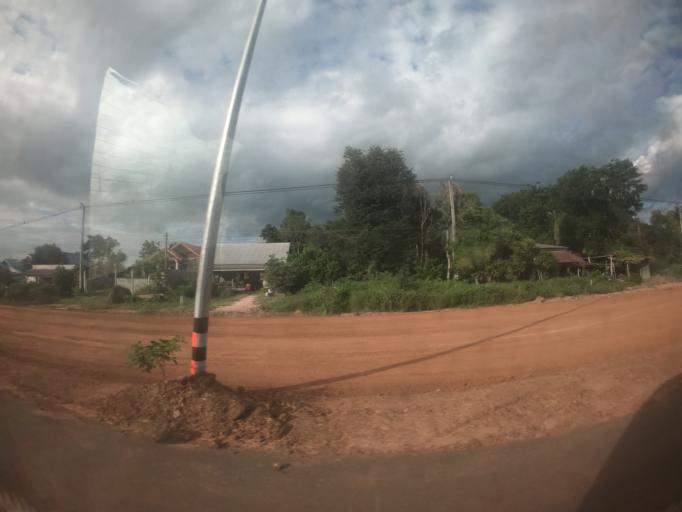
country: TH
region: Surin
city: Kap Choeng
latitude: 14.5005
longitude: 103.5635
